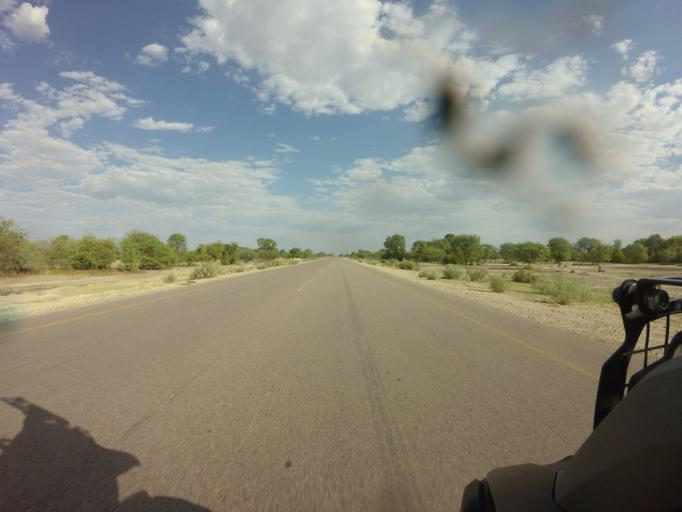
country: AO
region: Cunene
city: Ondjiva
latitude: -16.9899
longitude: 15.6260
